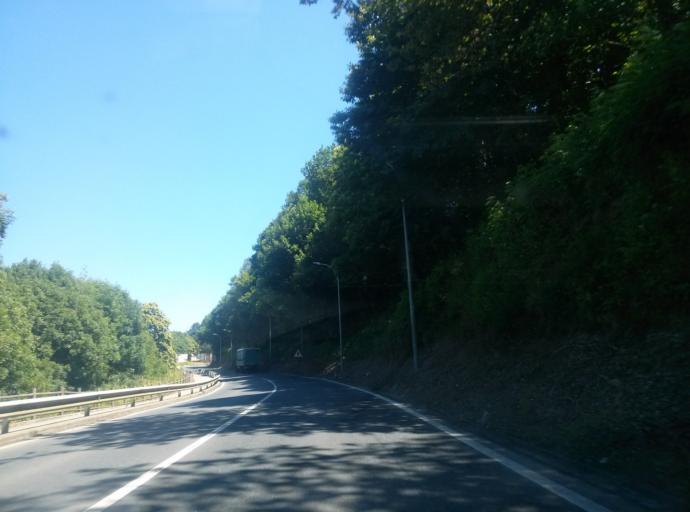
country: ES
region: Galicia
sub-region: Provincia de Lugo
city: Meira
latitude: 43.2149
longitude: -7.3023
